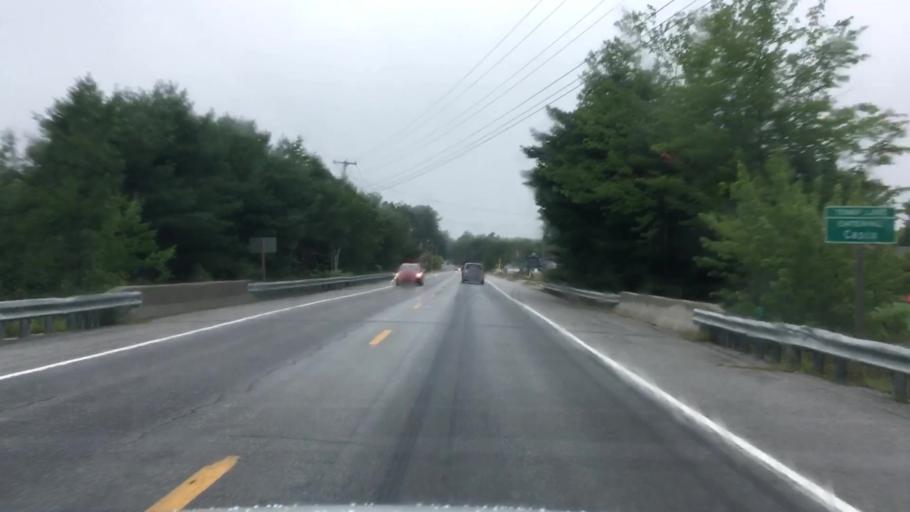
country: US
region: Maine
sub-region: Cumberland County
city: Raymond
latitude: 43.9115
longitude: -70.5091
